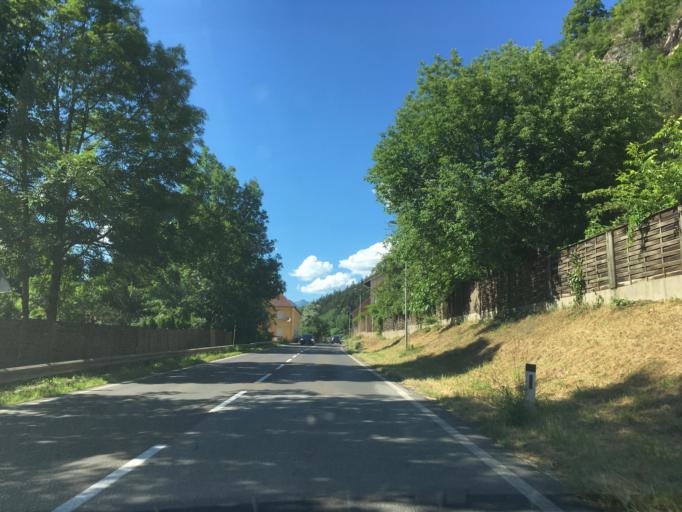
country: AT
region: Styria
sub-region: Politischer Bezirk Leoben
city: Sankt Peter-Freienstein
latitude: 47.4005
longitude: 15.0330
